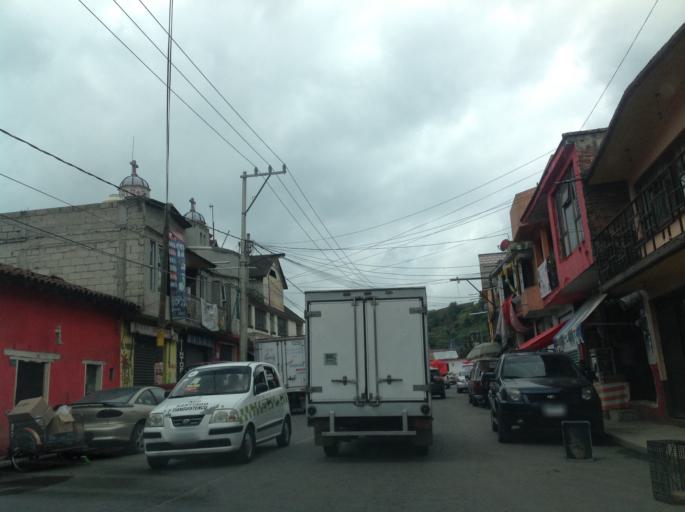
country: MX
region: Mexico
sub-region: Tenango del Valle
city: Santa Maria Jajalpa
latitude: 19.1125
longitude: -99.5368
